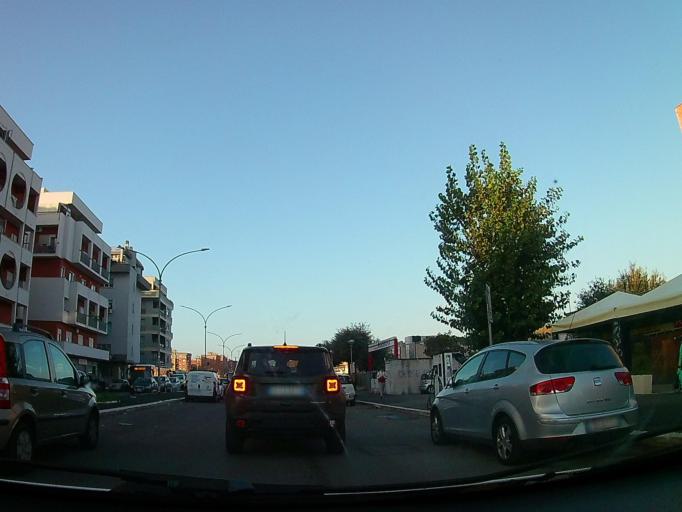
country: IT
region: Latium
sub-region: Citta metropolitana di Roma Capitale
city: Lido di Ostia
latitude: 41.7401
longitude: 12.2657
